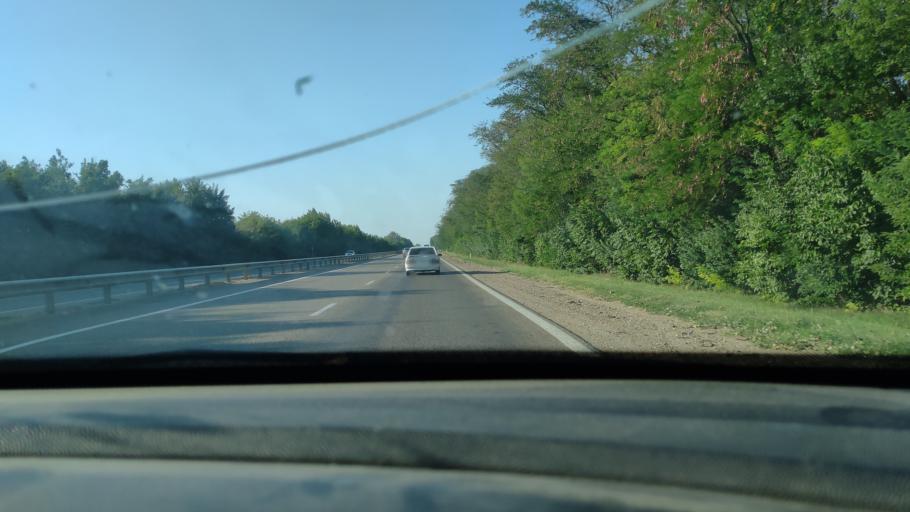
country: RU
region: Krasnodarskiy
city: Timashevsk
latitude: 45.5307
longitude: 38.9402
